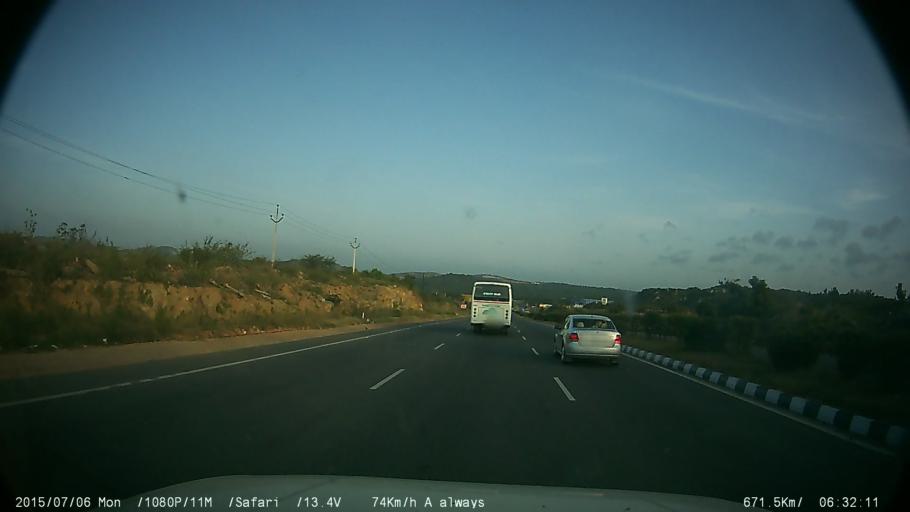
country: IN
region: Tamil Nadu
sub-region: Krishnagiri
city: Hosur
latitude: 12.6855
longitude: 77.9311
